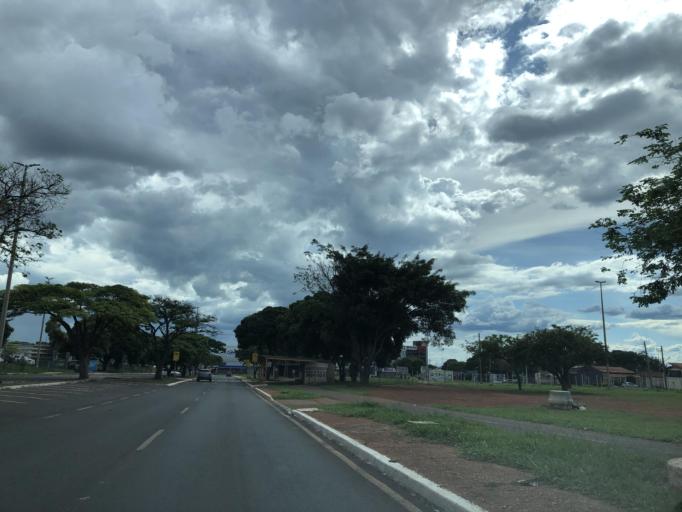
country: BR
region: Goias
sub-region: Luziania
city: Luziania
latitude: -16.0224
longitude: -48.0698
